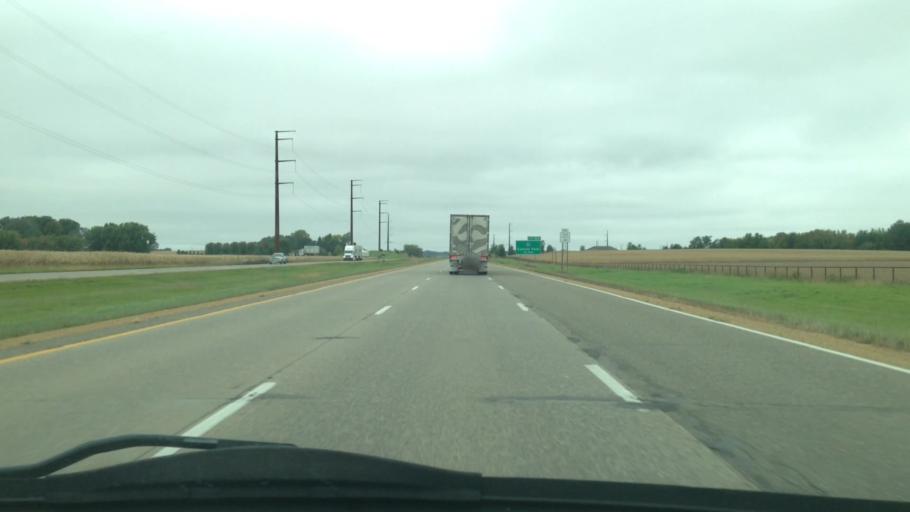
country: US
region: Minnesota
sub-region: Goodhue County
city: Cannon Falls
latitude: 44.5303
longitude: -92.9314
